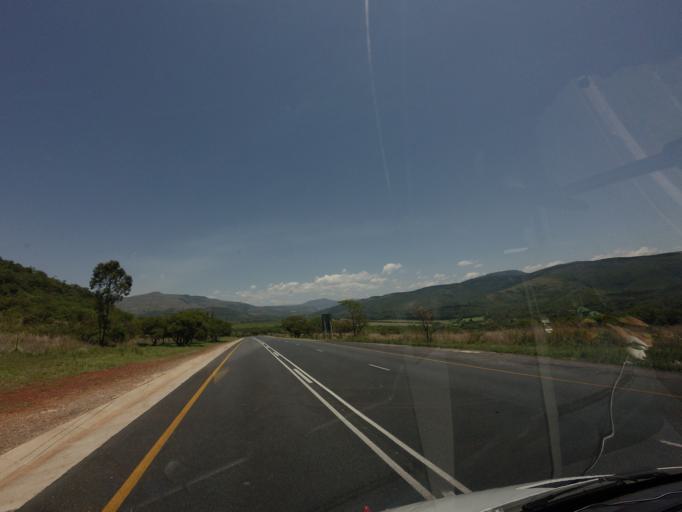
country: ZA
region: Mpumalanga
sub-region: Ehlanzeni District
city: Nelspruit
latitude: -25.4568
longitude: 30.6790
